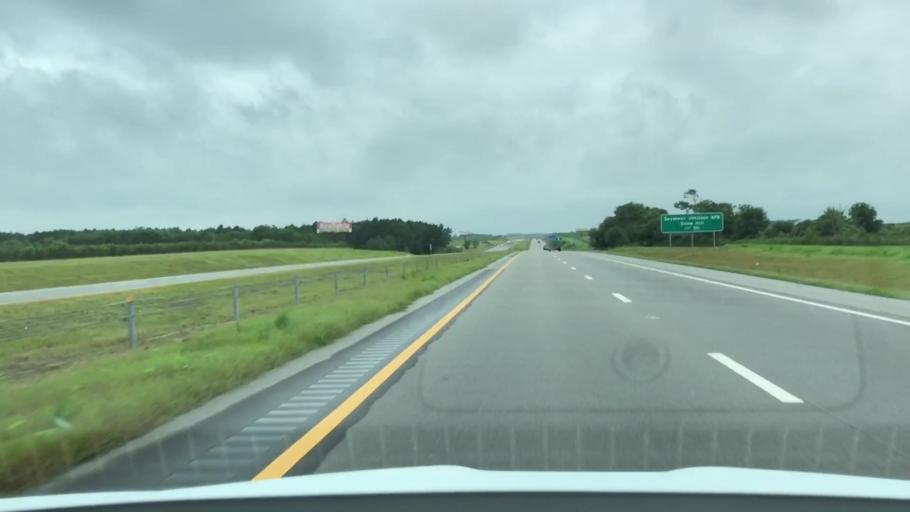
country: US
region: North Carolina
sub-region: Wayne County
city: Elroy
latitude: 35.4042
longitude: -77.8792
